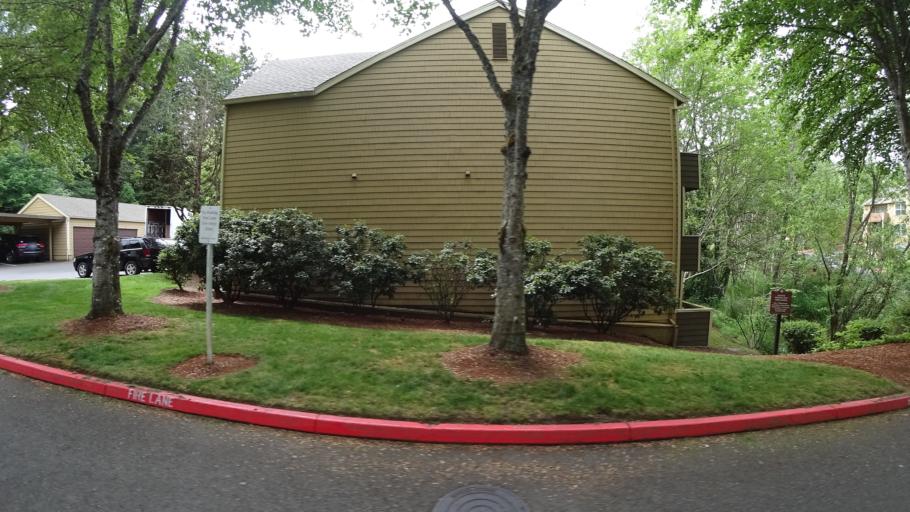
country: US
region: Oregon
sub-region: Washington County
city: Garden Home-Whitford
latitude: 45.4718
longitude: -122.7540
